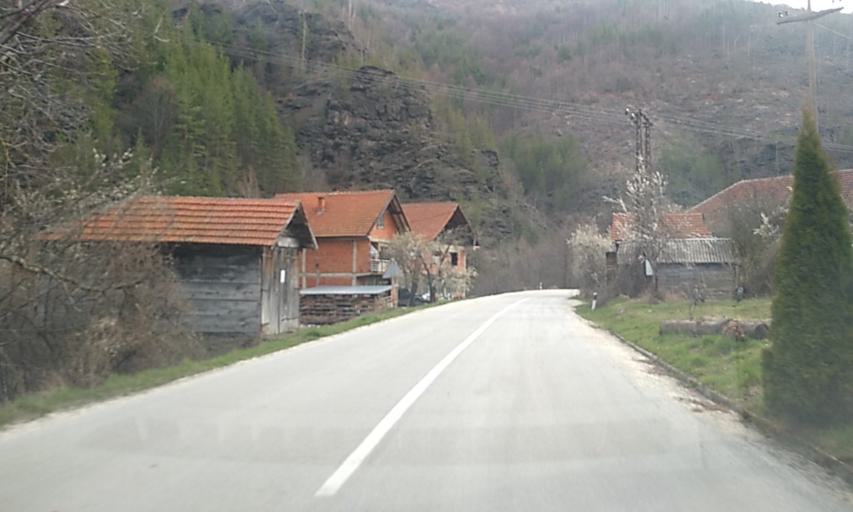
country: RS
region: Central Serbia
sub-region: Pcinjski Okrug
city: Bosilegrad
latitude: 42.5420
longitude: 22.4067
